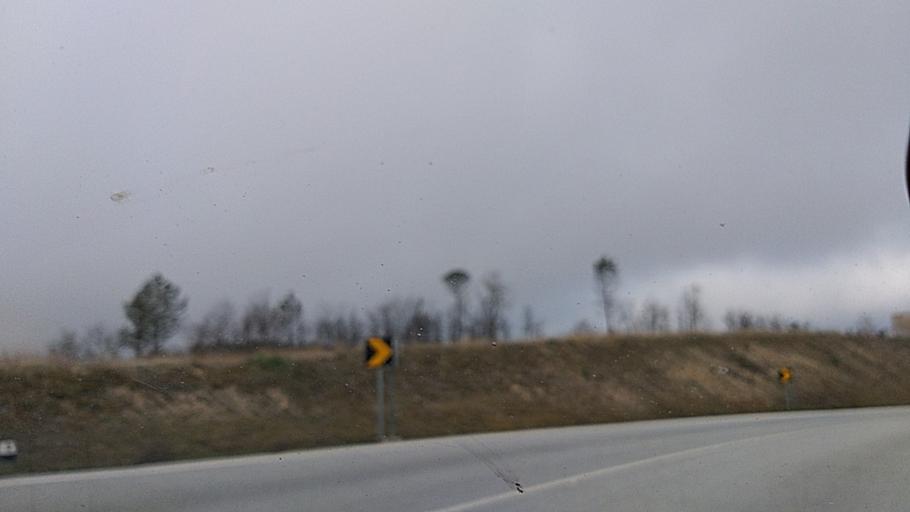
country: PT
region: Guarda
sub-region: Fornos de Algodres
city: Fornos de Algodres
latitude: 40.7009
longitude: -7.4843
